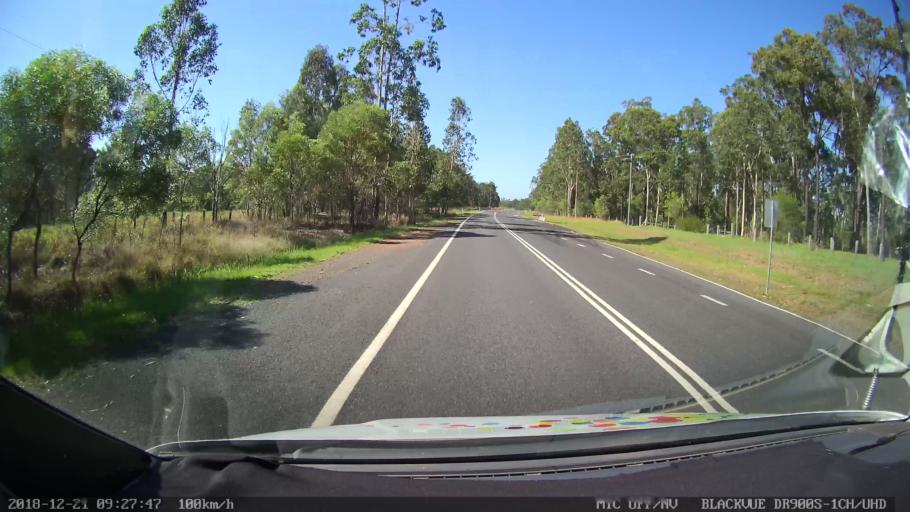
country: AU
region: New South Wales
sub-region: Clarence Valley
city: Maclean
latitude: -29.4079
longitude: 152.9886
